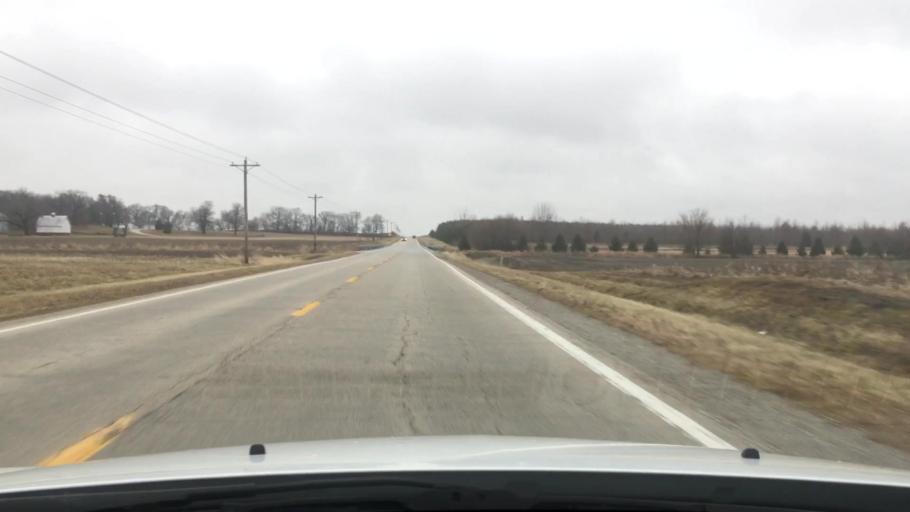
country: US
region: Illinois
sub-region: Iroquois County
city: Watseka
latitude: 40.8909
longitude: -87.6807
